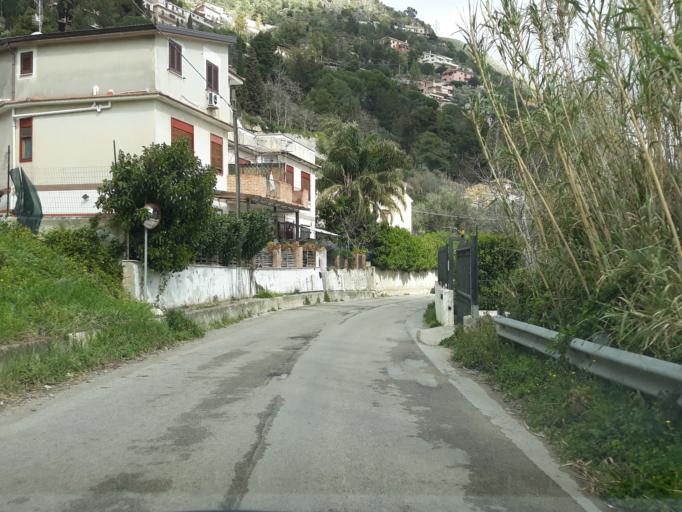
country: IT
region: Sicily
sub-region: Palermo
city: Monreale
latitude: 38.0861
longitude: 13.2979
